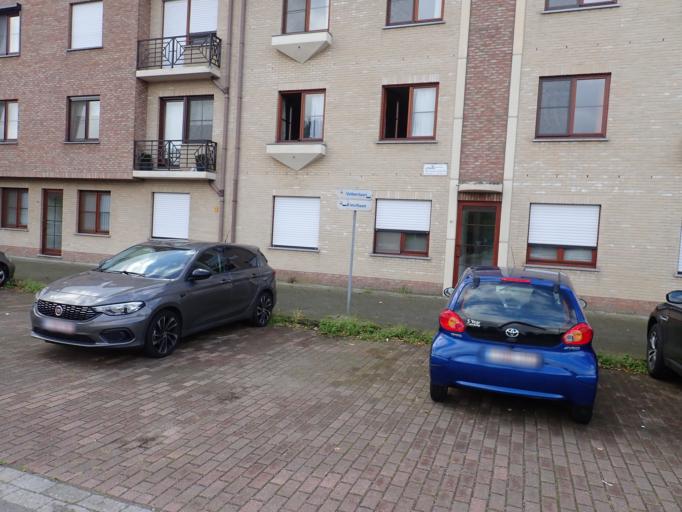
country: BE
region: Flanders
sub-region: Provincie Antwerpen
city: Ranst
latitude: 51.1880
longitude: 4.5569
